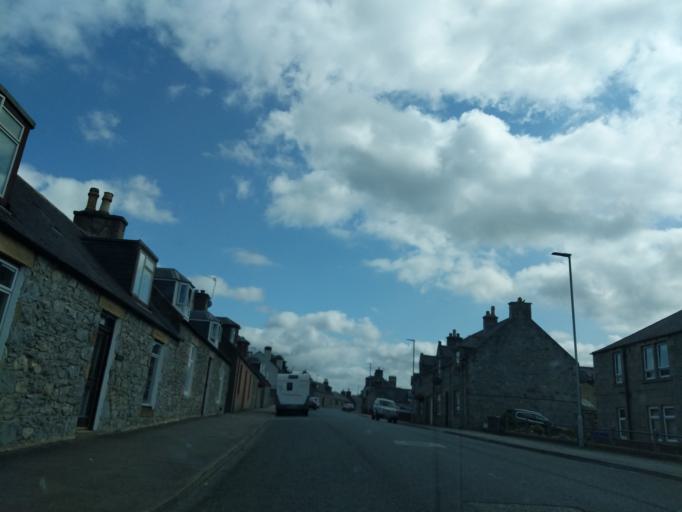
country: GB
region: Scotland
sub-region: Moray
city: Dufftown
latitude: 57.4491
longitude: -3.1304
